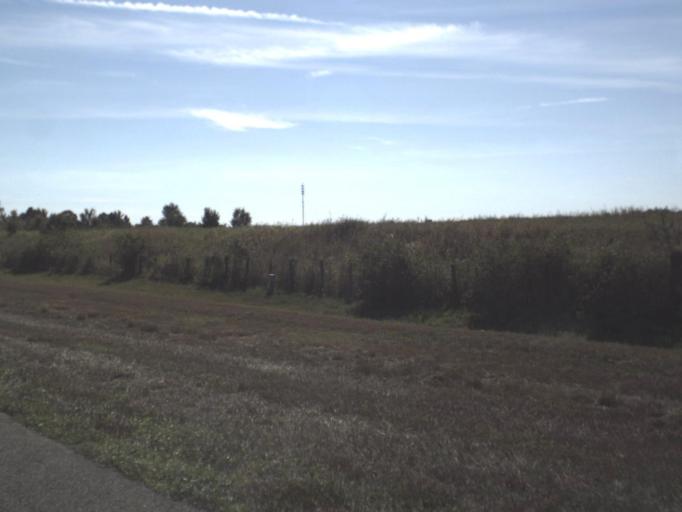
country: US
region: Florida
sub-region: Highlands County
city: Placid Lakes
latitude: 27.0801
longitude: -81.3351
